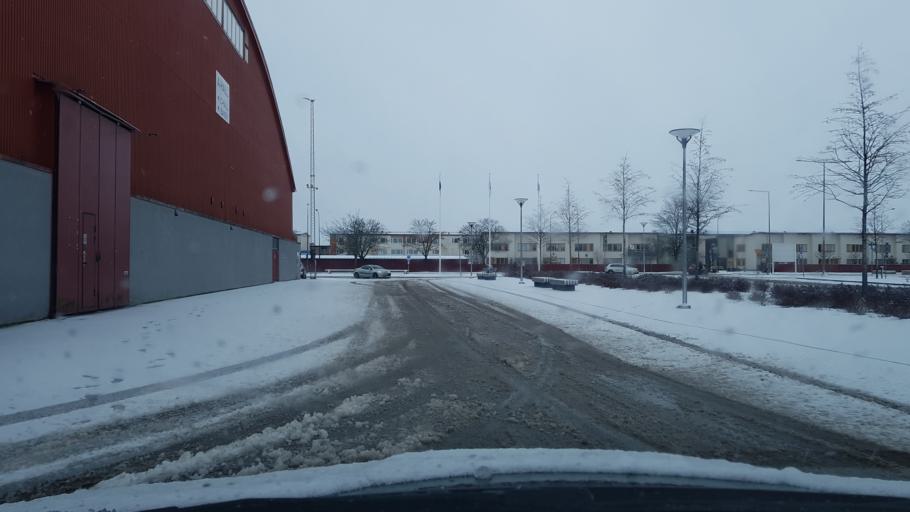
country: SE
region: Uppsala
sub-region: Uppsala Kommun
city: Uppsala
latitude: 59.8808
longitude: 17.6572
